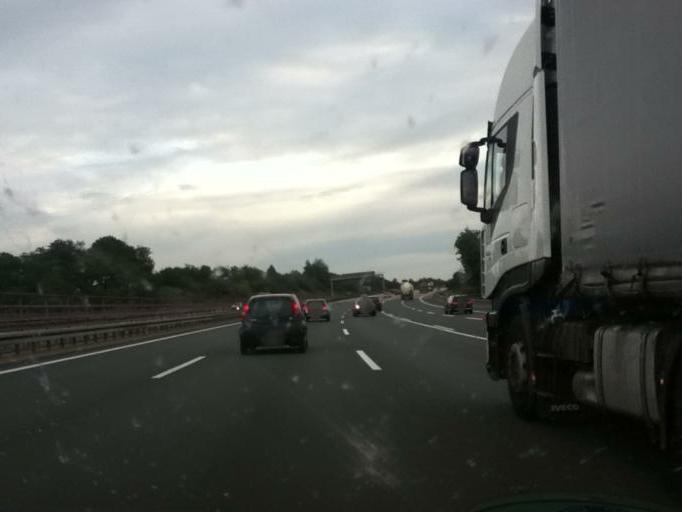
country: DE
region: Saxony
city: Reinsberg
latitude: 51.0585
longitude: 13.3801
